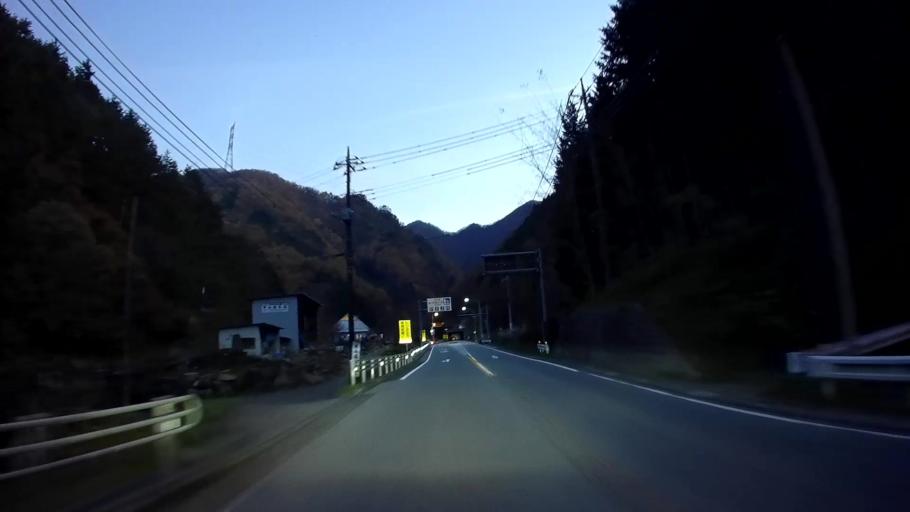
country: JP
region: Yamanashi
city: Enzan
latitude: 35.6375
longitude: 138.7918
